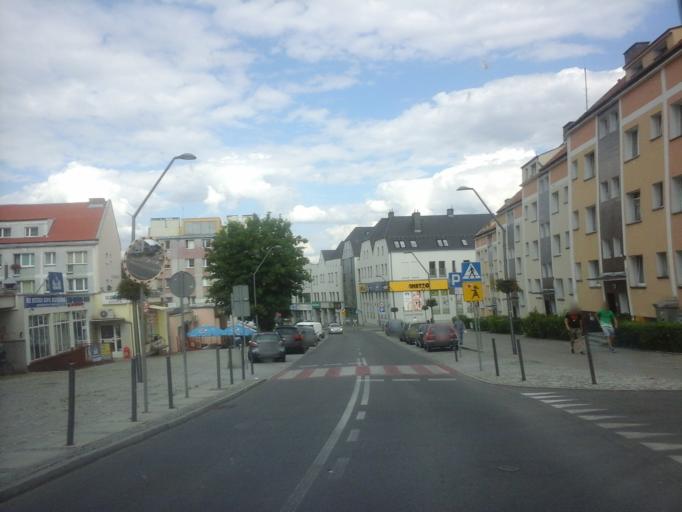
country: PL
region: West Pomeranian Voivodeship
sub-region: Powiat stargardzki
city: Stargard Szczecinski
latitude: 53.3390
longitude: 15.0424
